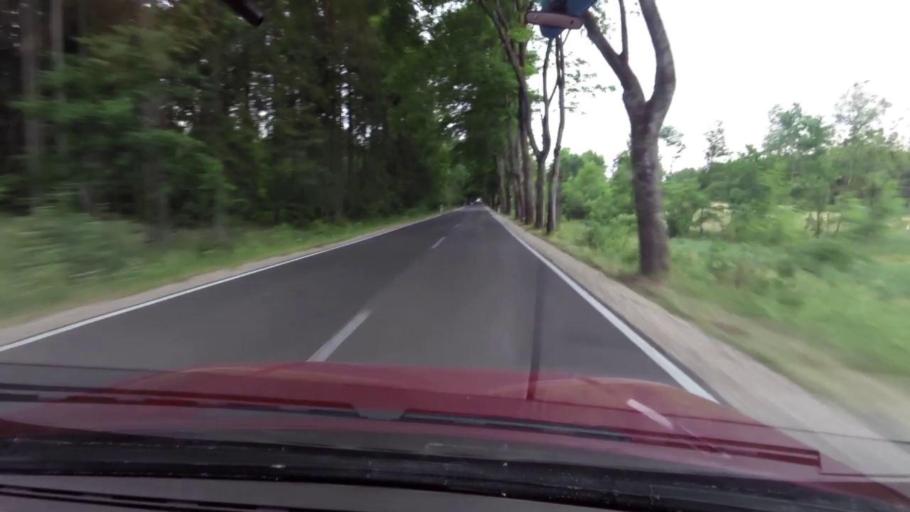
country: PL
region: West Pomeranian Voivodeship
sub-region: Powiat koszalinski
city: Sianow
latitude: 54.1528
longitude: 16.4658
